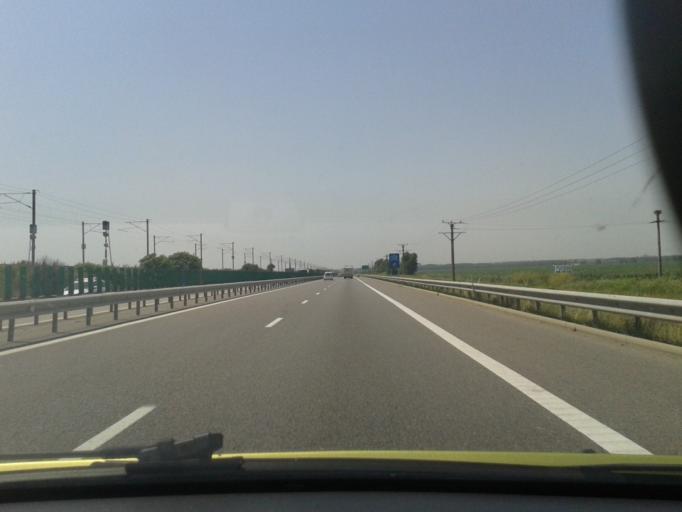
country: RO
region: Ialomita
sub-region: Comuna Stelnica
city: Stelnica
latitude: 44.3664
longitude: 27.9130
